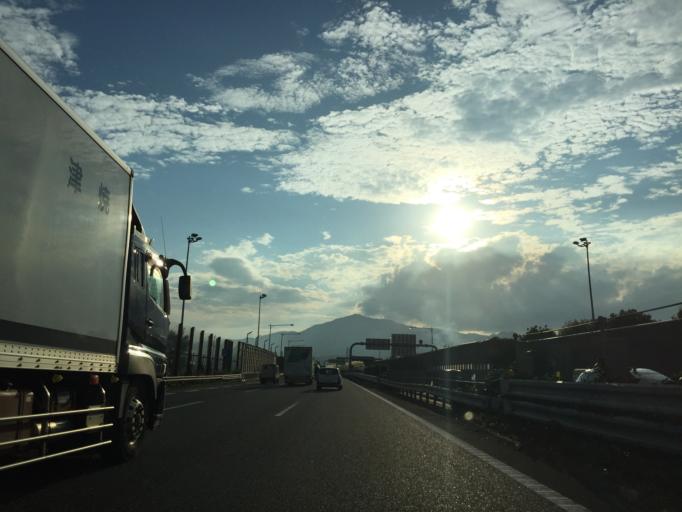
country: JP
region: Kanagawa
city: Atsugi
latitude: 35.4246
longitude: 139.3569
